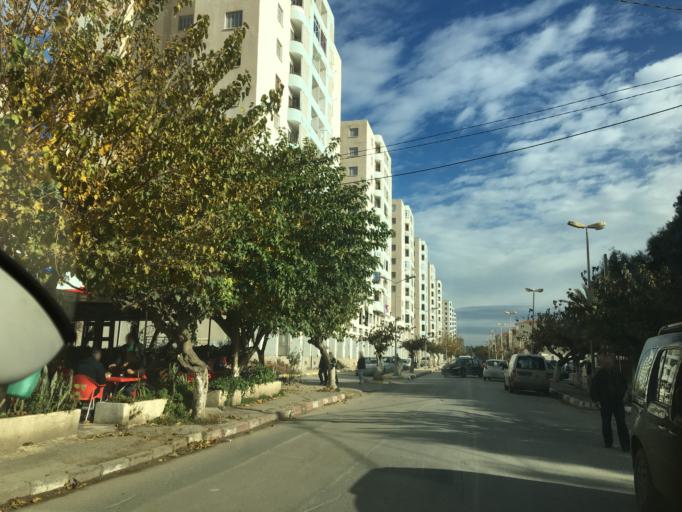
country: DZ
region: Alger
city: Ain Taya
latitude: 36.7915
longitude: 3.2385
